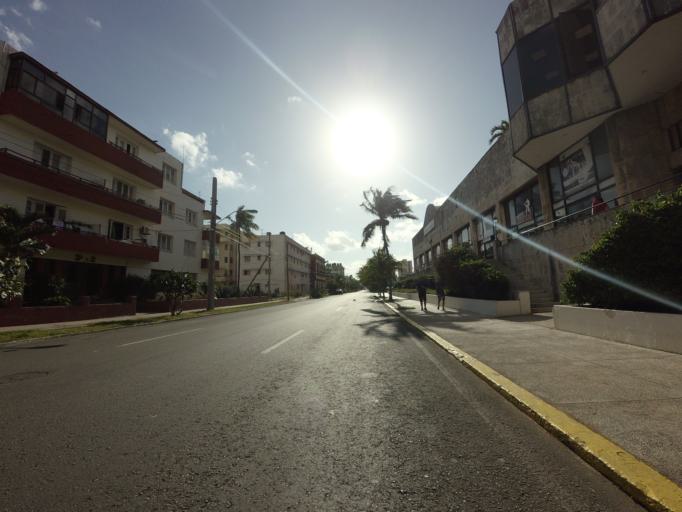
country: CU
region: La Habana
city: Havana
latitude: 23.1391
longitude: -82.4026
